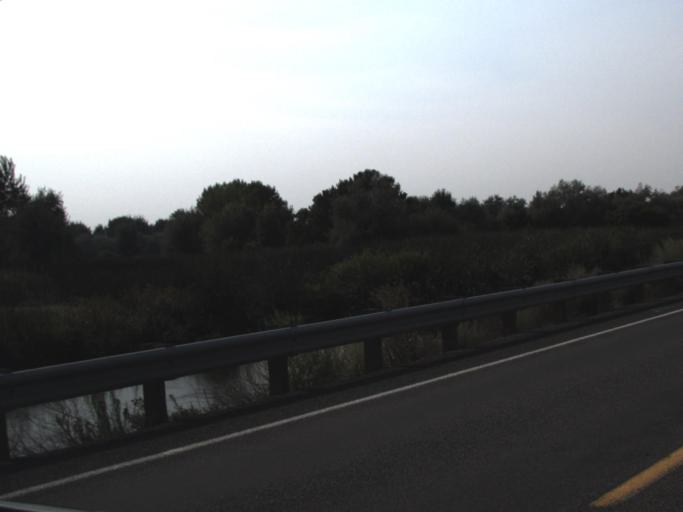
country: US
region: Washington
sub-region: Yakima County
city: Granger
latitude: 46.3179
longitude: -120.2213
